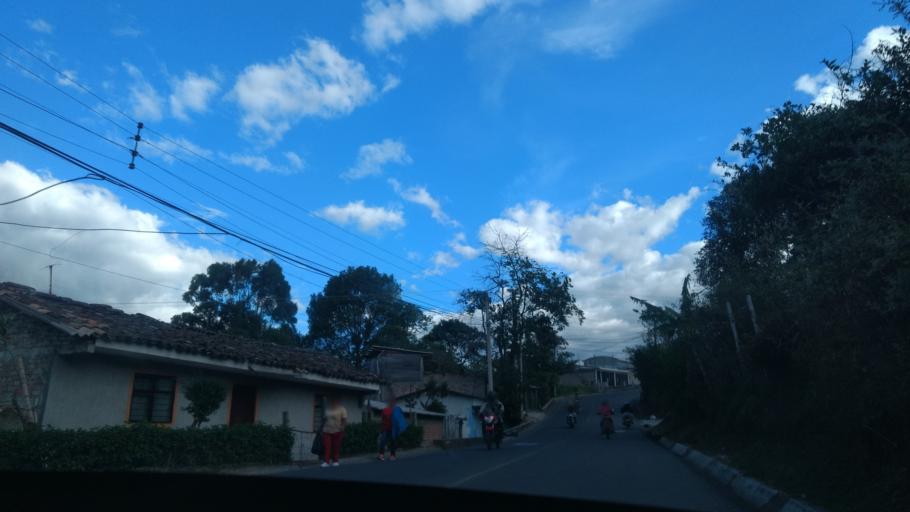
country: CO
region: Cauca
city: Popayan
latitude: 2.4859
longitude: -76.5774
